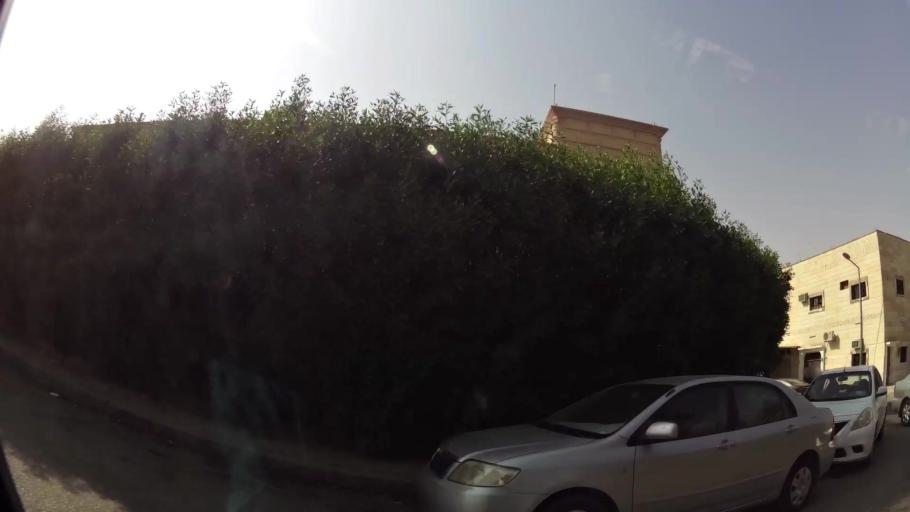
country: KW
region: Muhafazat al Jahra'
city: Al Jahra'
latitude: 29.3464
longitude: 47.6576
